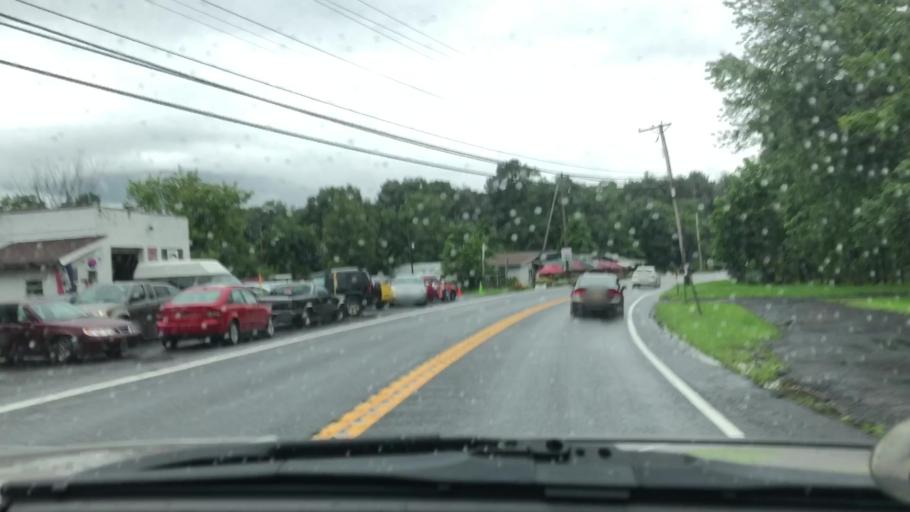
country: US
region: New York
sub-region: Ulster County
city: Manorville
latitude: 42.1352
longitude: -74.0006
